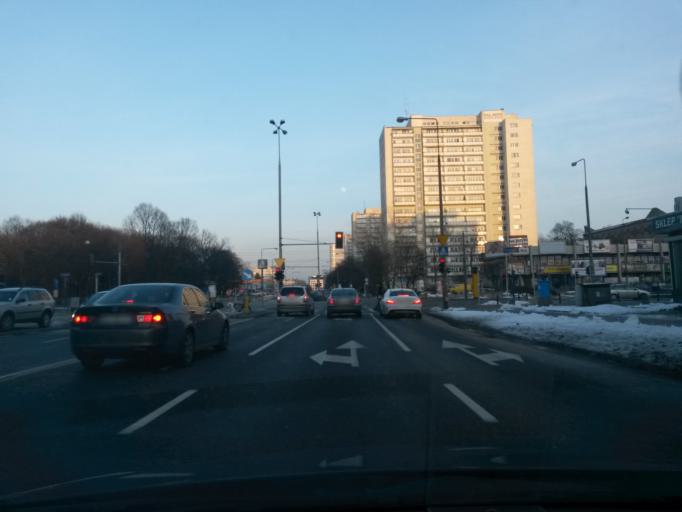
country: PL
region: Masovian Voivodeship
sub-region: Warszawa
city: Warsaw
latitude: 52.2104
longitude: 21.0061
